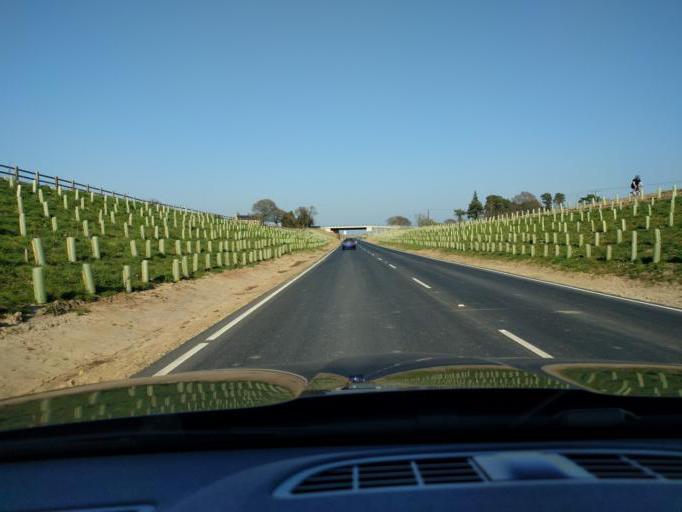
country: GB
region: England
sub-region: Northumberland
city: Morpeth
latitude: 55.1801
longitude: -1.7063
